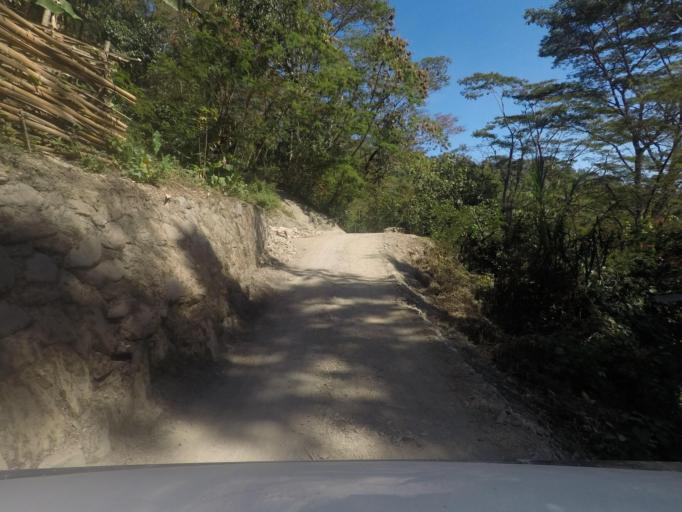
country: TL
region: Ermera
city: Gleno
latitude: -8.7275
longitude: 125.3343
